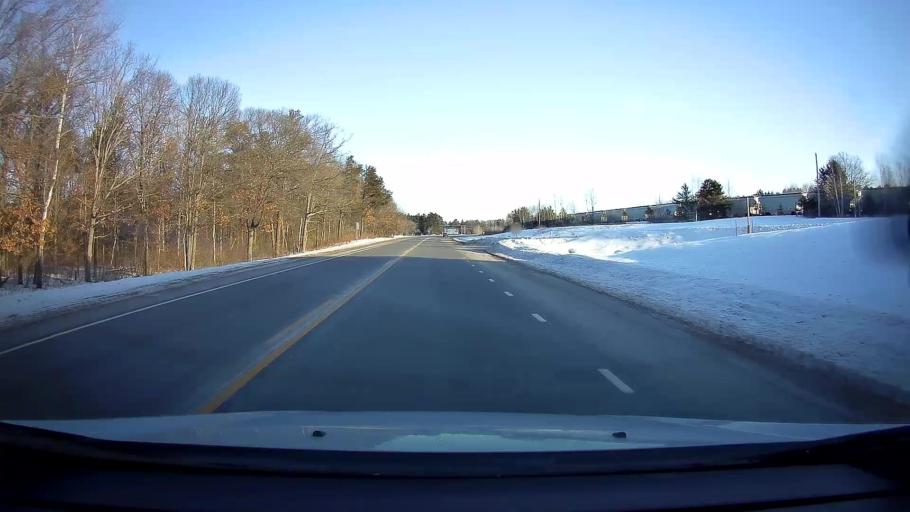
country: US
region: Wisconsin
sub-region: Washburn County
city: Spooner
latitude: 45.8381
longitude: -91.8806
